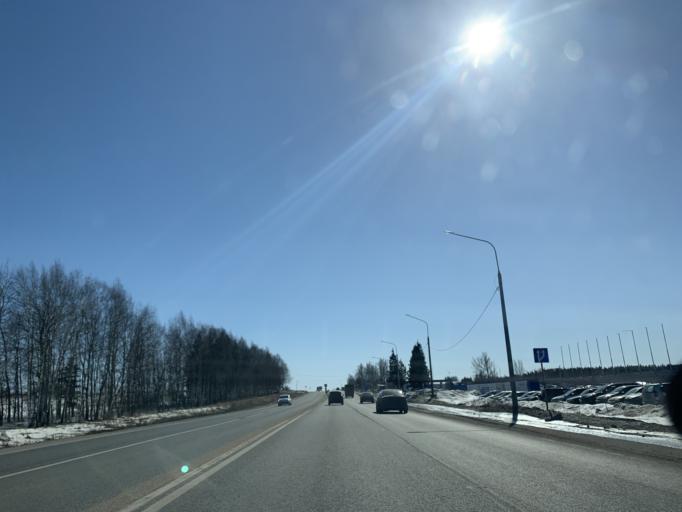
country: RU
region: Jaroslavl
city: Tutayev
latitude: 57.8516
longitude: 39.5460
